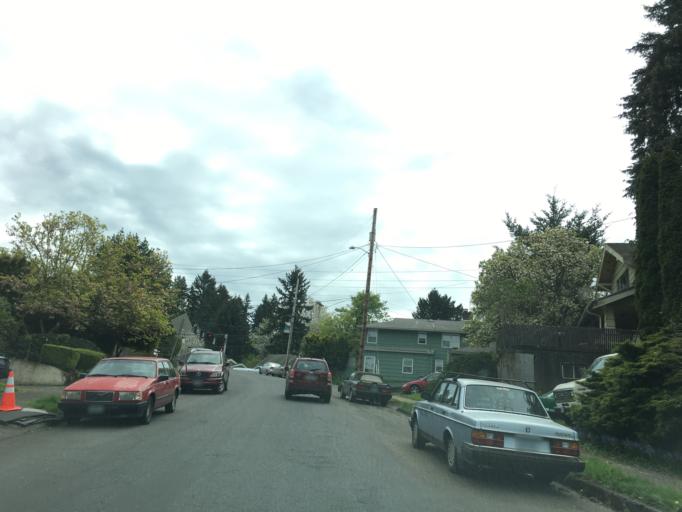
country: US
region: Oregon
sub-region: Multnomah County
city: Lents
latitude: 45.5239
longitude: -122.5943
